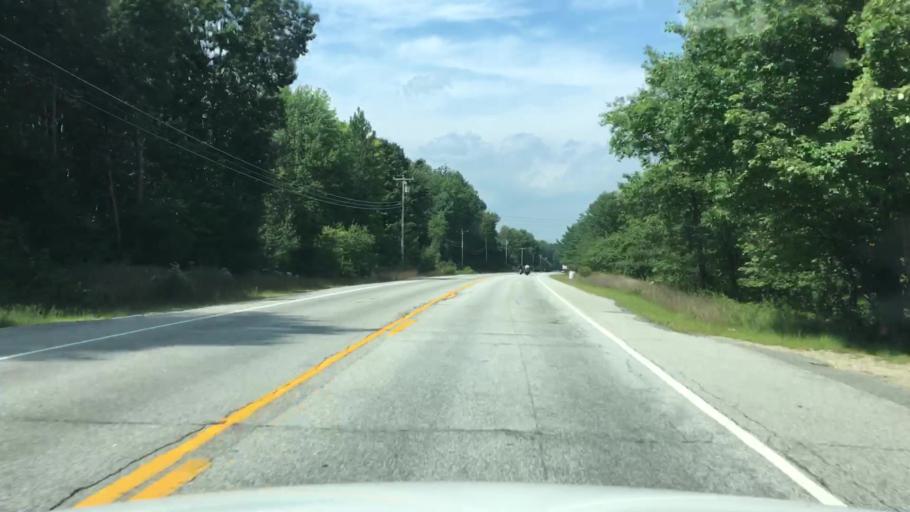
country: US
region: Maine
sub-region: Oxford County
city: Peru
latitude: 44.4966
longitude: -70.3918
